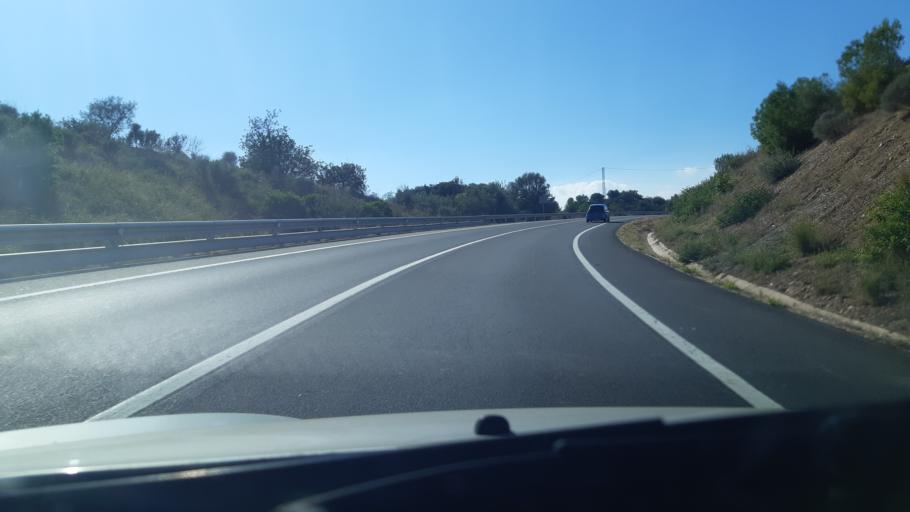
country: ES
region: Catalonia
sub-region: Provincia de Tarragona
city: Tivenys
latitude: 40.9150
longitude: 0.4930
